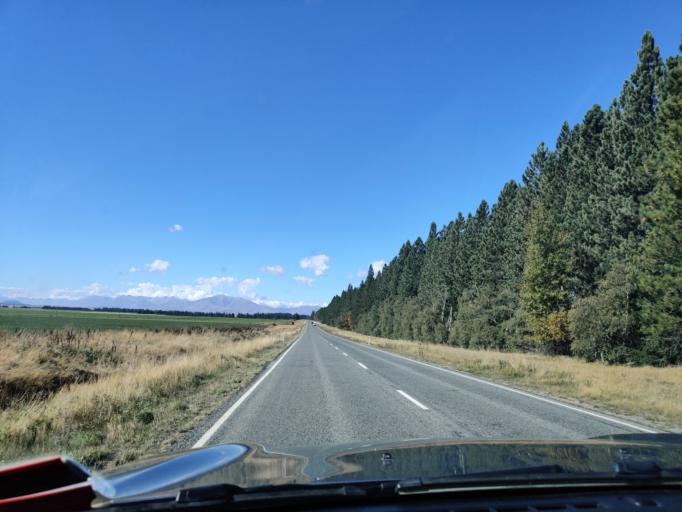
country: NZ
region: Canterbury
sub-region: Timaru District
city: Pleasant Point
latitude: -44.1920
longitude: 170.2905
